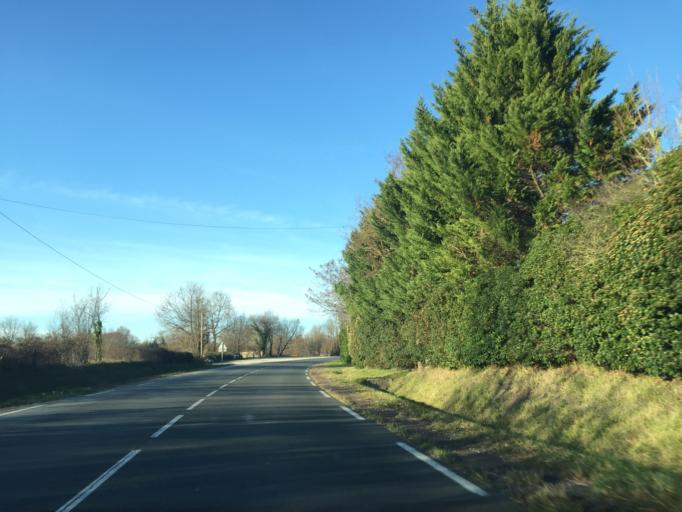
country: FR
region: Aquitaine
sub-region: Departement de la Dordogne
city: Riberac
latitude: 45.1943
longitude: 0.3699
